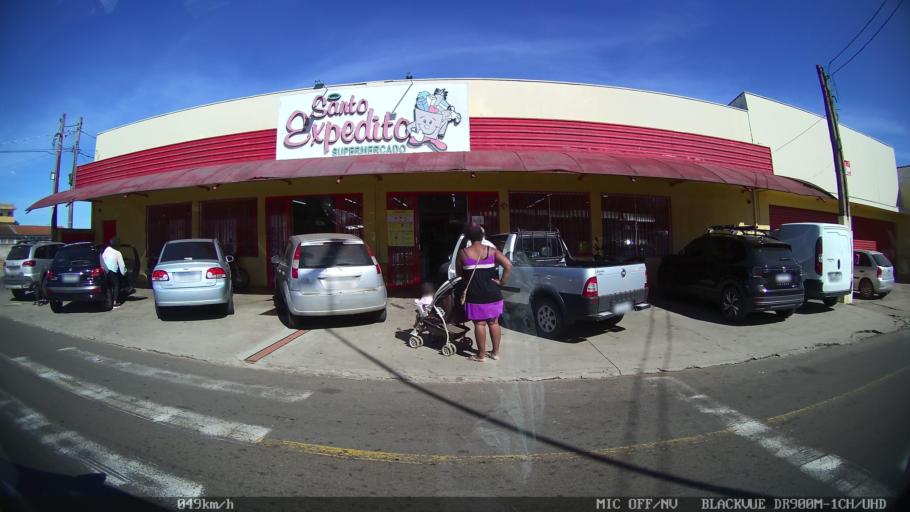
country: BR
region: Sao Paulo
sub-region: Franca
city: Franca
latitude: -20.5349
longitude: -47.3650
